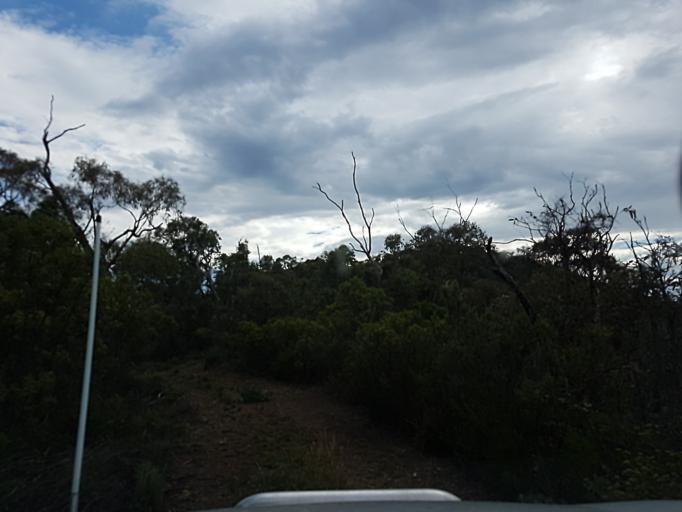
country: AU
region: New South Wales
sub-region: Snowy River
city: Jindabyne
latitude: -36.9990
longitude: 148.4036
